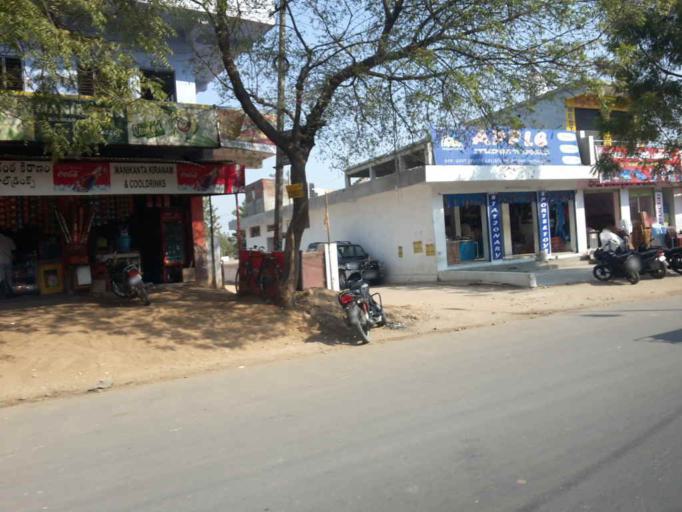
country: IN
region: Telangana
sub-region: Karimnagar
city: Koratla
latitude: 18.8489
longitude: 78.6194
